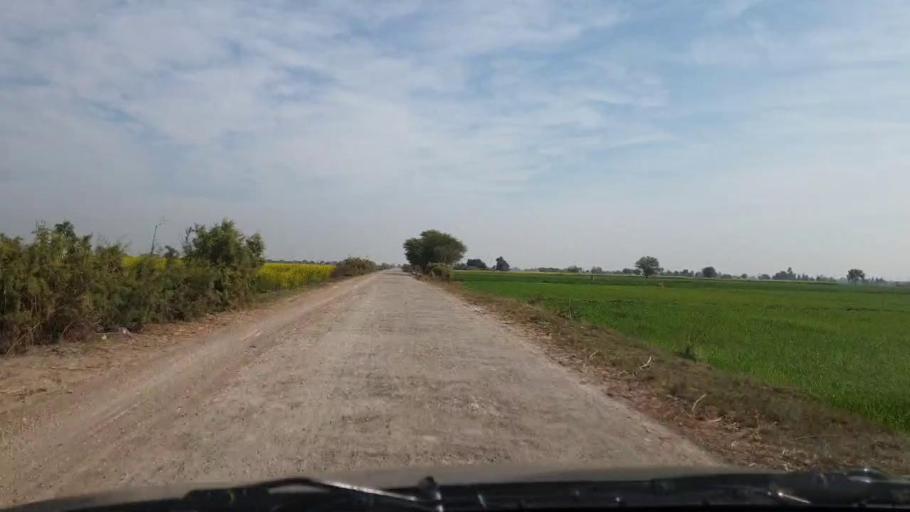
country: PK
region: Sindh
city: Jam Sahib
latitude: 26.2689
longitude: 68.6967
